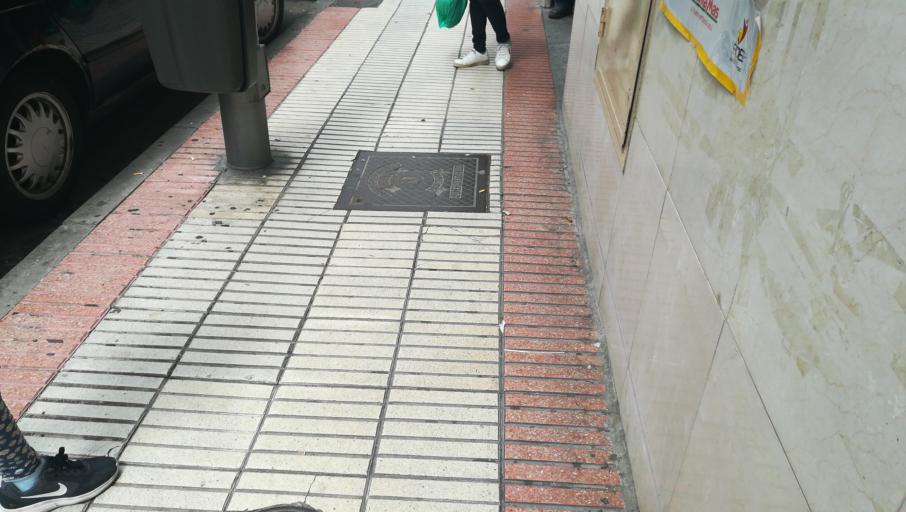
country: ES
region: Madrid
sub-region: Provincia de Madrid
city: Retiro
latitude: 40.4167
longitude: -3.6734
